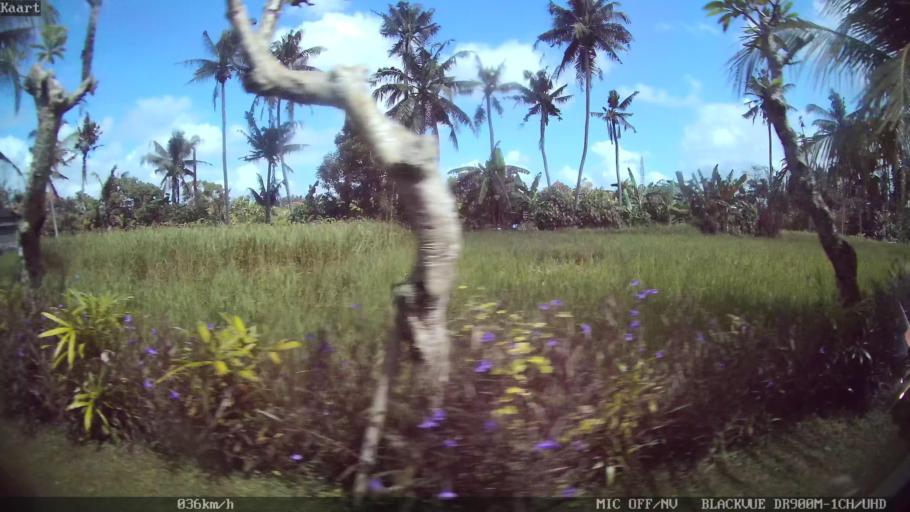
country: ID
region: Bali
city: Banjar Tebongkang
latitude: -8.5496
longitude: 115.2752
